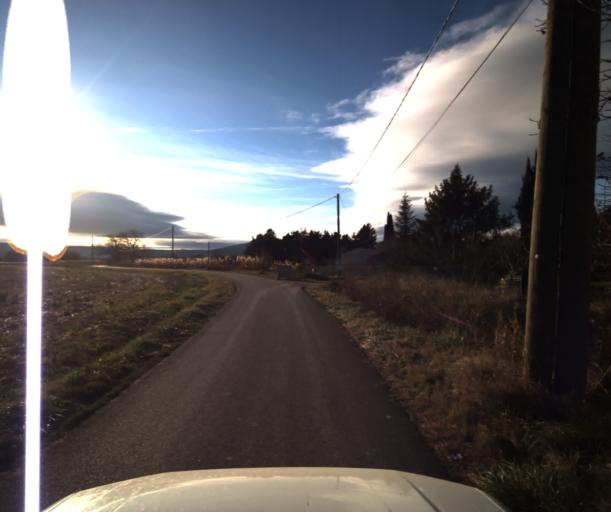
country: FR
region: Provence-Alpes-Cote d'Azur
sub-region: Departement du Vaucluse
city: Villelaure
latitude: 43.6927
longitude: 5.4615
